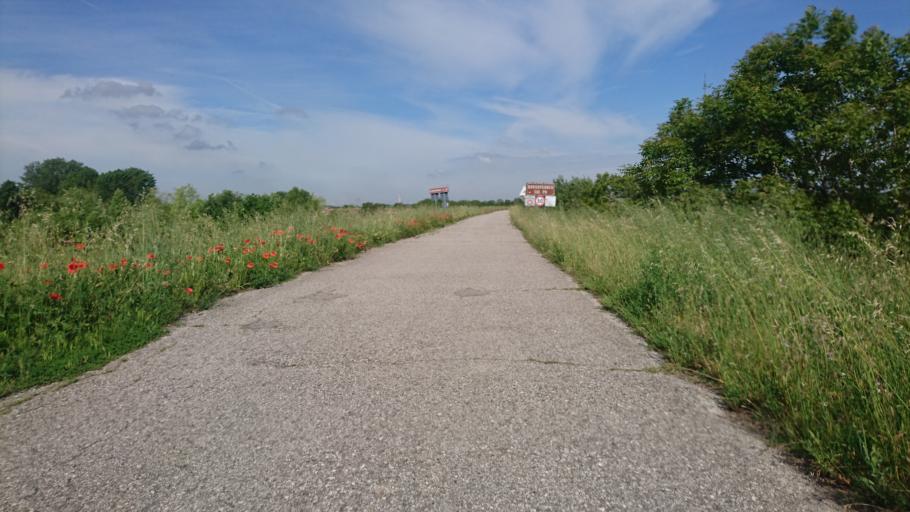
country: IT
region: Lombardy
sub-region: Provincia di Mantova
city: Carbonara di Po
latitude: 45.0407
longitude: 11.2211
